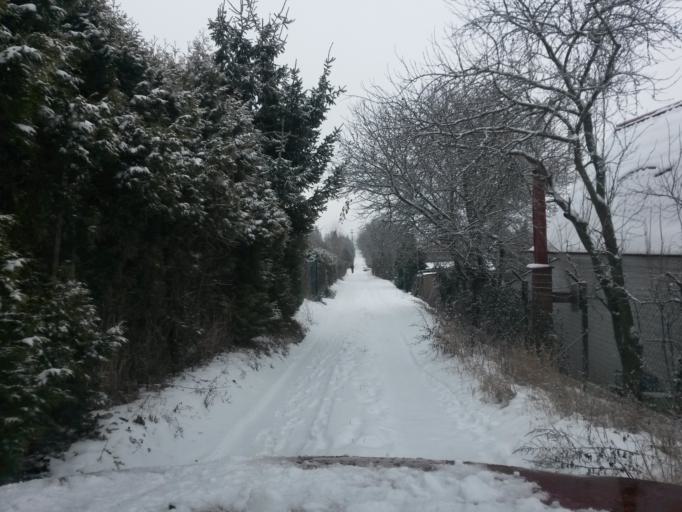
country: SK
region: Kosicky
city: Kosice
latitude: 48.7159
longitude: 21.3175
